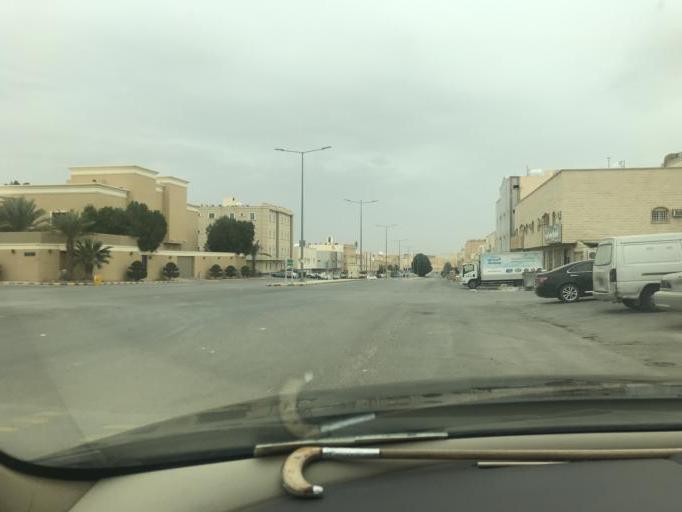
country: SA
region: Ar Riyad
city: Riyadh
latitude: 24.7788
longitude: 46.6977
